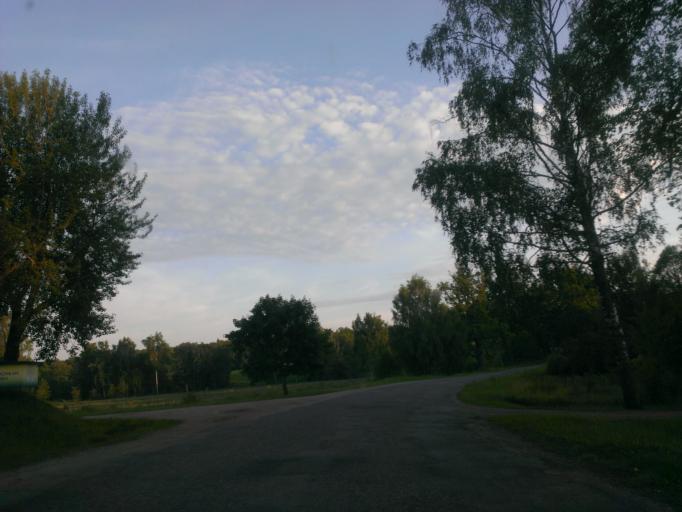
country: LV
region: Amatas Novads
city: Drabesi
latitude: 57.2500
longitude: 25.2797
